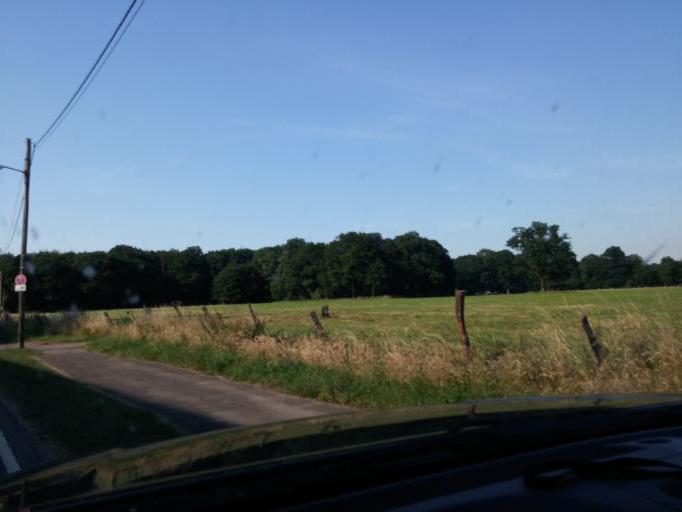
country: DE
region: North Rhine-Westphalia
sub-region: Regierungsbezirk Dusseldorf
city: Monchengladbach
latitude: 51.1563
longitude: 6.3781
